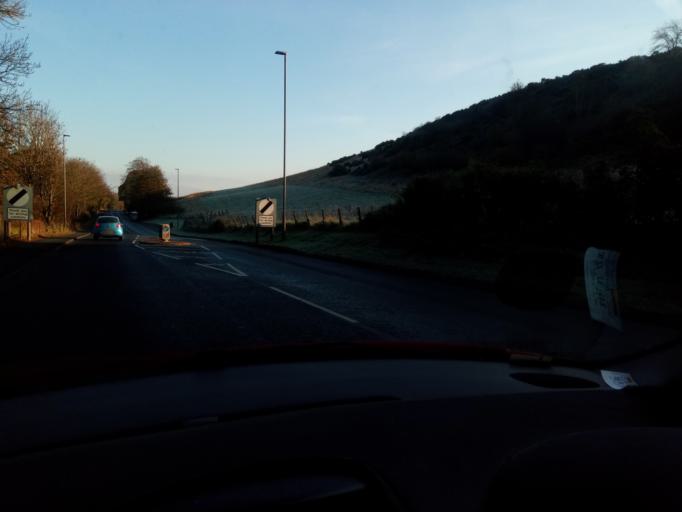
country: GB
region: Scotland
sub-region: The Scottish Borders
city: Hawick
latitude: 55.4331
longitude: -2.7591
